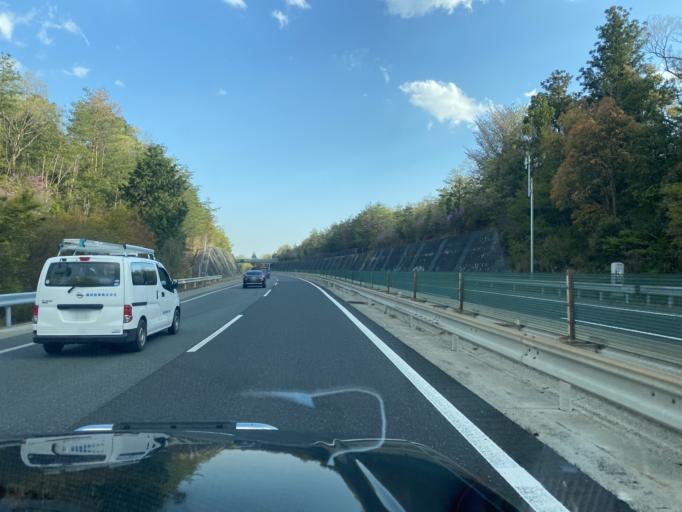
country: JP
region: Hyogo
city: Sandacho
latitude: 34.9150
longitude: 135.1540
